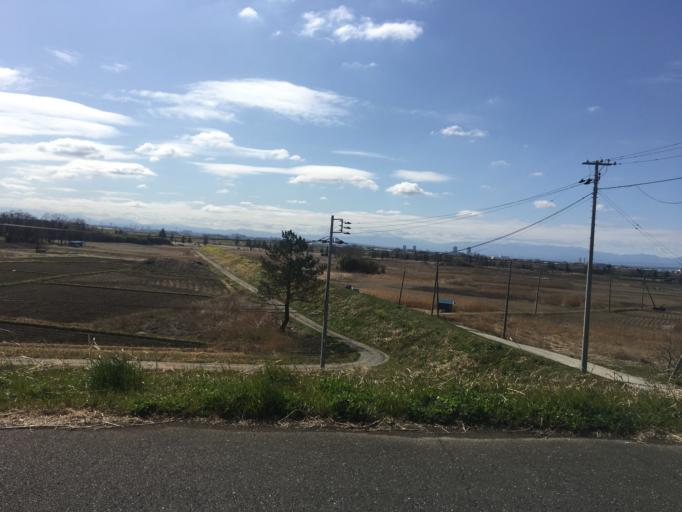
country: JP
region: Saitama
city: Shiki
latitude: 35.8686
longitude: 139.5889
